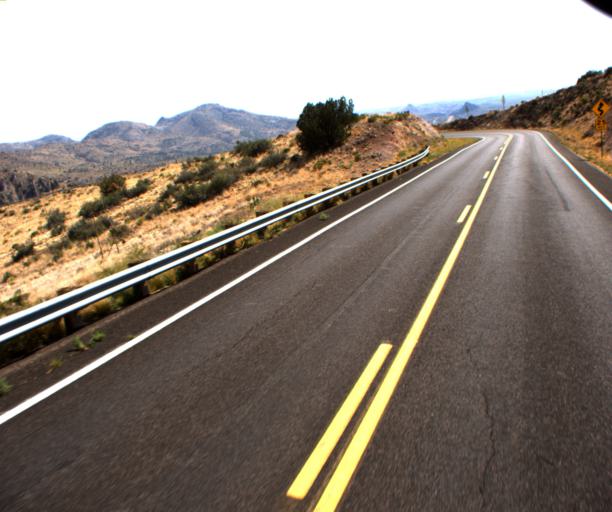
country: US
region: Arizona
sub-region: Greenlee County
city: Clifton
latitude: 33.0512
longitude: -109.1017
